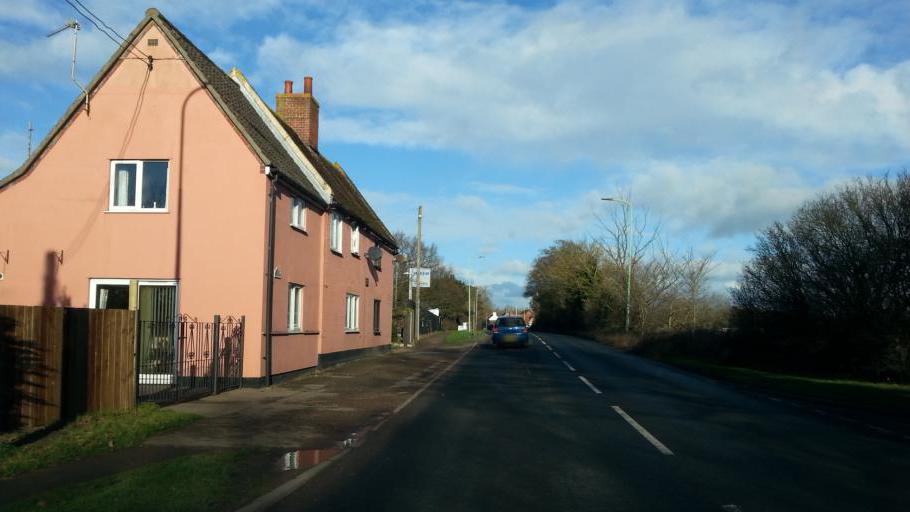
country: GB
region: England
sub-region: Suffolk
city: Halesworth
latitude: 52.3533
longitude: 1.5105
